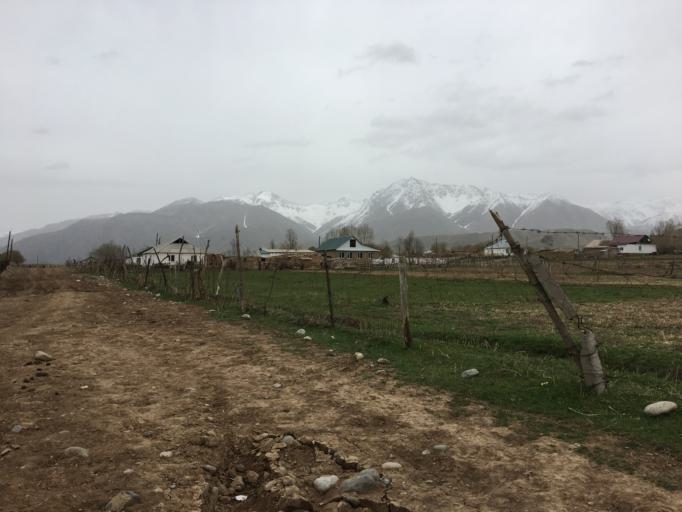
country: KG
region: Naryn
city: Naryn
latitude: 41.5183
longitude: 76.4358
